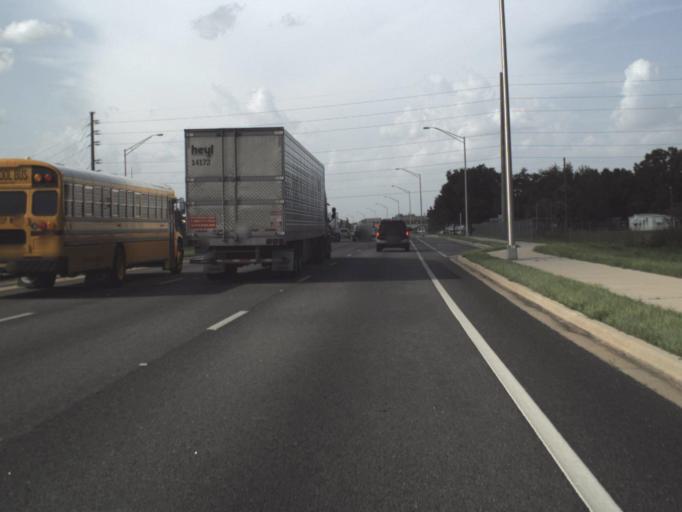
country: US
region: Florida
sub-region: Polk County
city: Dundee
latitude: 28.0099
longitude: -81.6313
